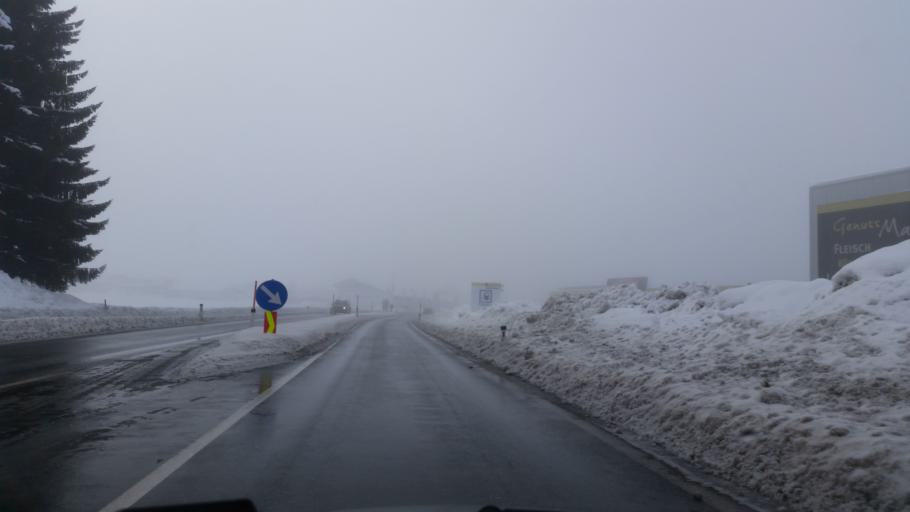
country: AT
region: Tyrol
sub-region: Politischer Bezirk Kitzbuhel
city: Kirchdorf in Tirol
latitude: 47.5400
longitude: 12.4442
